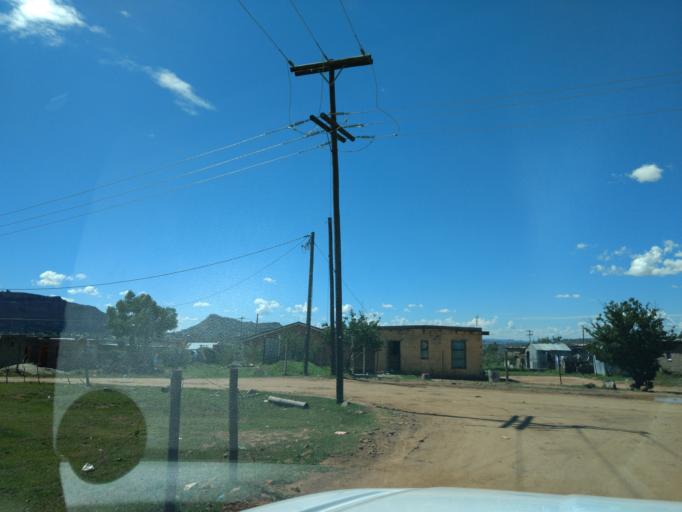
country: LS
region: Maseru
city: Maseru
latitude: -29.3684
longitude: 27.5122
